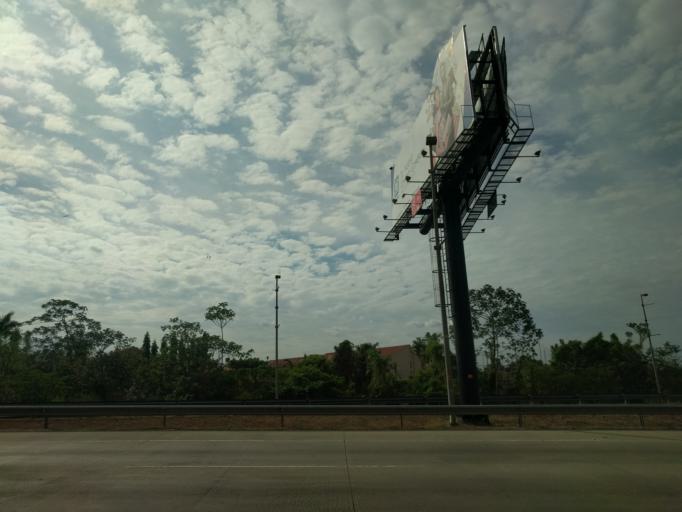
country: PA
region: Panama
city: San Miguelito
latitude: 9.0241
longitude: -79.4694
